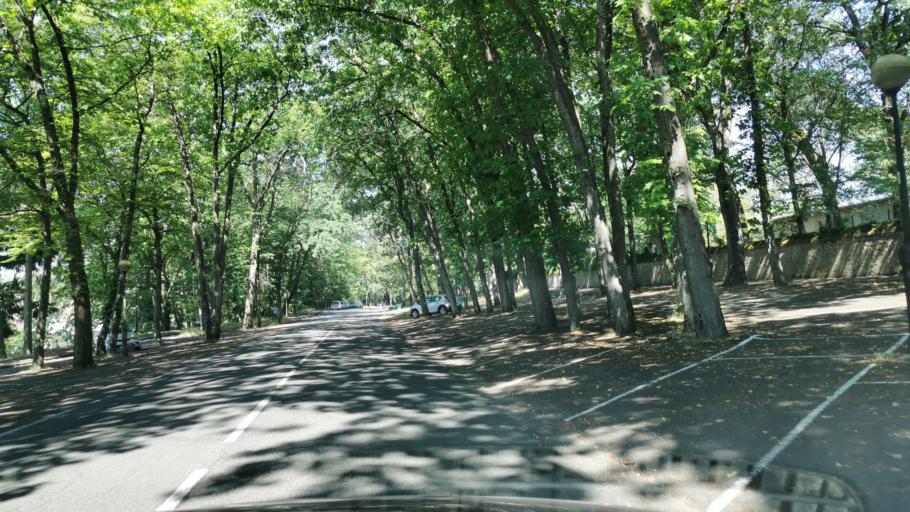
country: FR
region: Bourgogne
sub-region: Departement de Saone-et-Loire
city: Le Creusot
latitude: 46.7999
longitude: 4.4250
